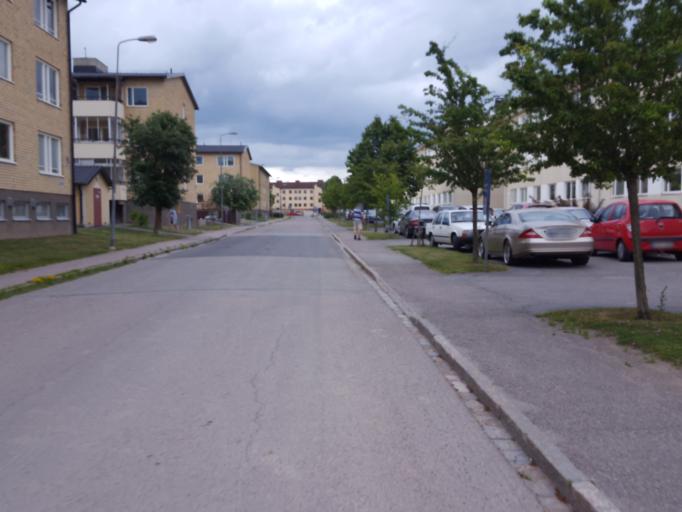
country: SE
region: Uppsala
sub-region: Uppsala Kommun
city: Uppsala
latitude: 59.8721
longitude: 17.6625
